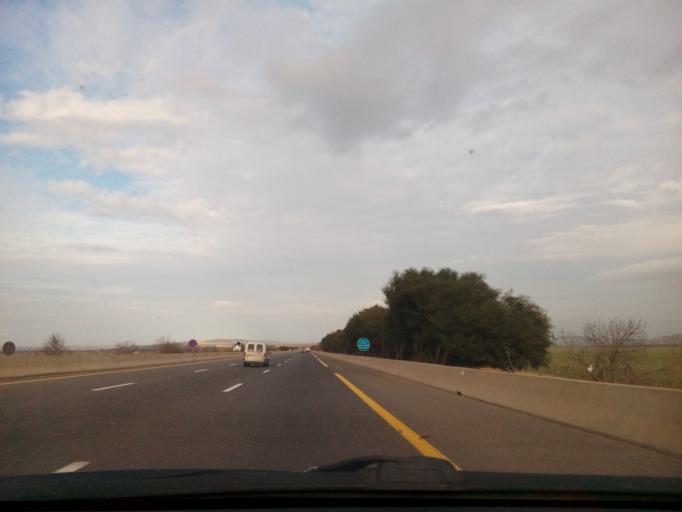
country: DZ
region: Mostaganem
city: Mostaganem
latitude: 35.6756
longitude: 0.1493
